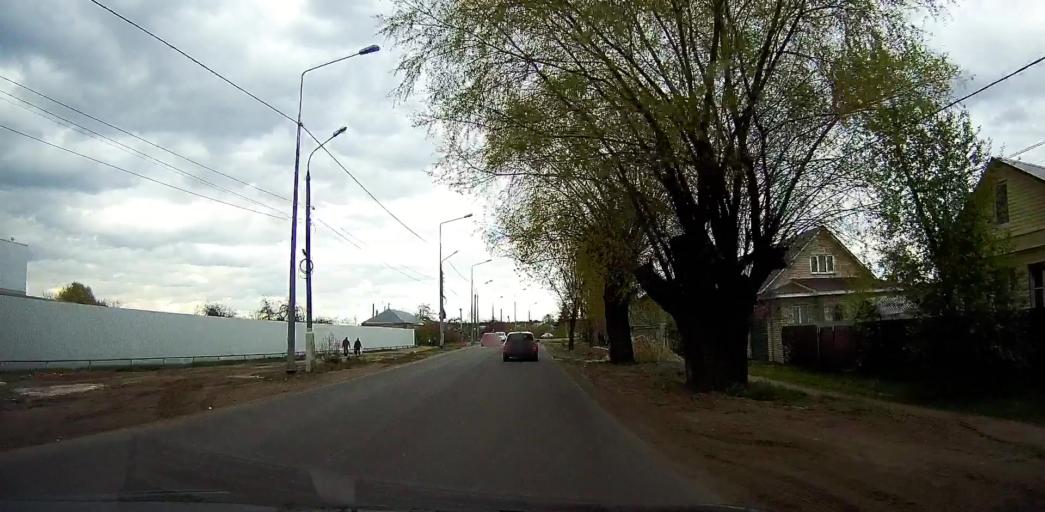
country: RU
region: Moskovskaya
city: Pavlovskiy Posad
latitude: 55.7721
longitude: 38.6895
